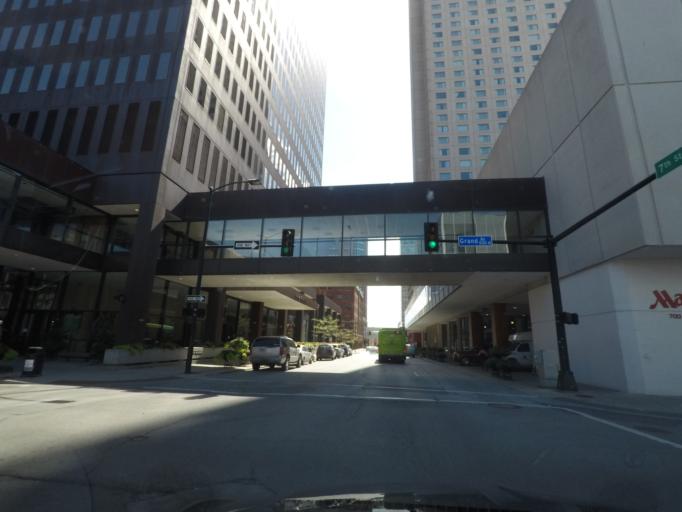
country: US
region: Iowa
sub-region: Polk County
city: Des Moines
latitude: 41.5876
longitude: -93.6266
